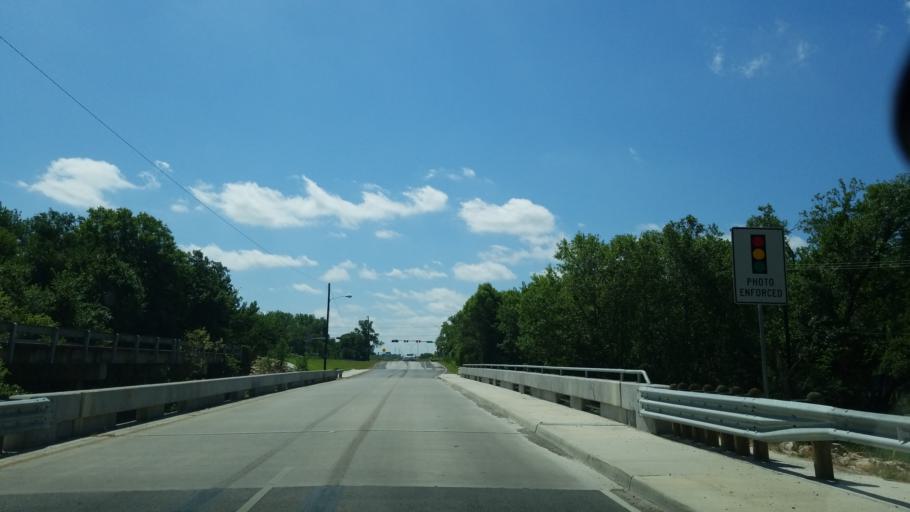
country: US
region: Texas
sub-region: Dallas County
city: Dallas
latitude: 32.7488
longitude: -96.7303
